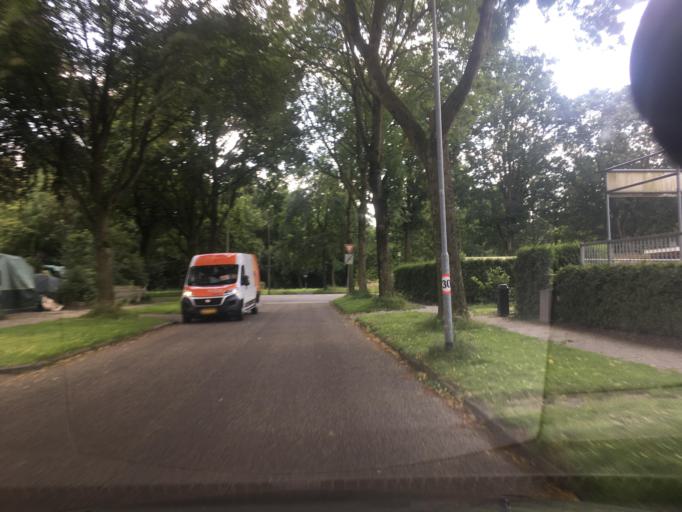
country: NL
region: Groningen
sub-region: Gemeente Hoogezand-Sappemeer
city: Sappemeer
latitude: 53.1552
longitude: 6.7868
